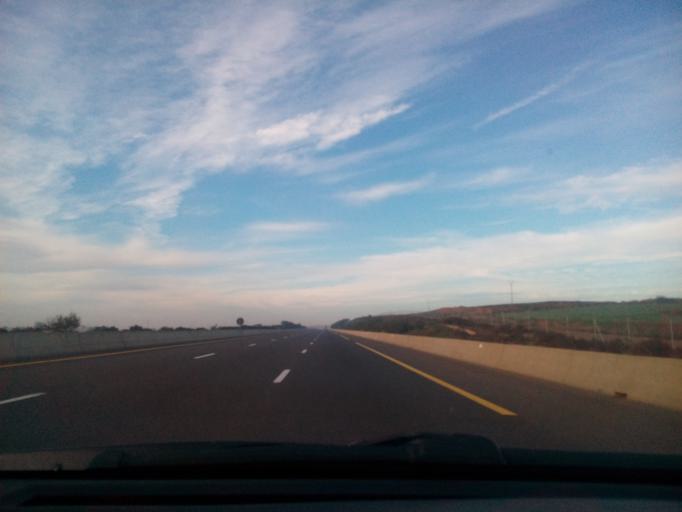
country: DZ
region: Relizane
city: Relizane
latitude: 35.7156
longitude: 0.2884
